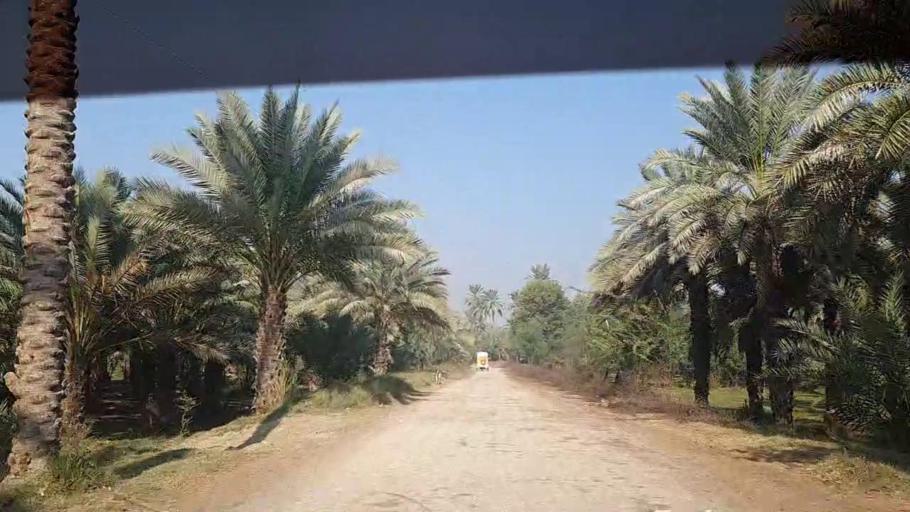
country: PK
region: Sindh
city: Khairpur
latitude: 27.4904
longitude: 68.7404
